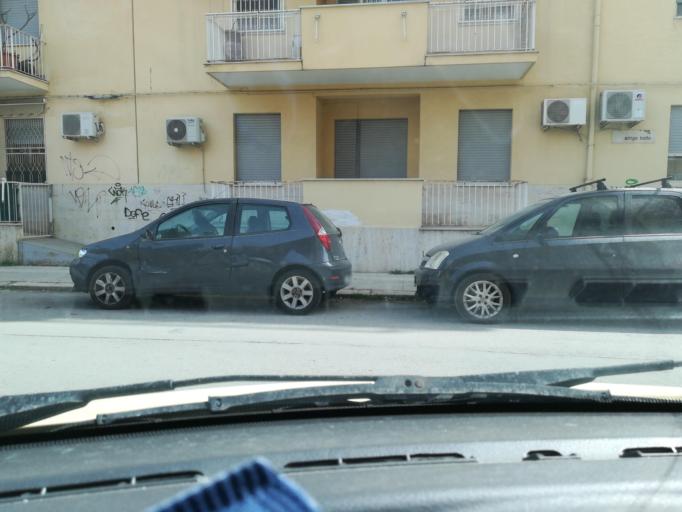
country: IT
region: Sicily
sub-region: Palermo
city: Palermo
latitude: 38.1309
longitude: 13.3406
